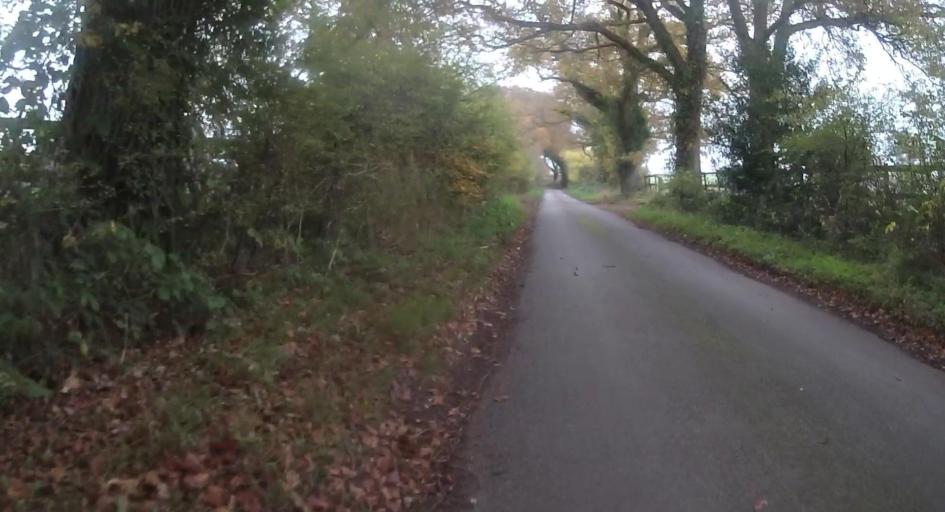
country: GB
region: England
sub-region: Wokingham
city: Finchampstead
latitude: 51.3724
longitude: -0.8758
